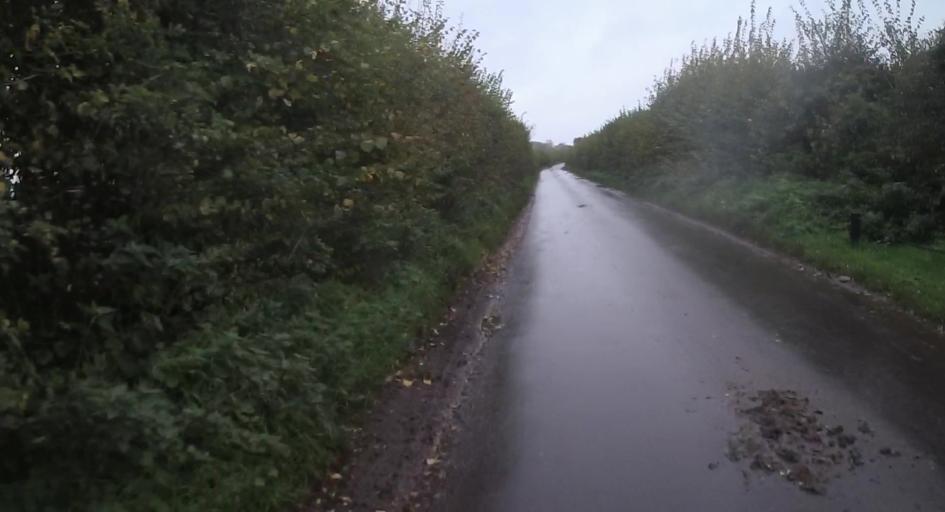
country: GB
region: England
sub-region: Surrey
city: Farnham
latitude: 51.2073
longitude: -0.8534
